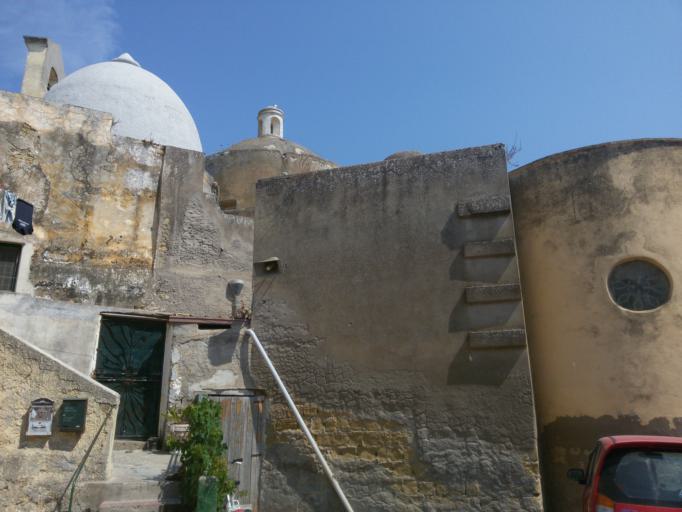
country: IT
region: Campania
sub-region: Provincia di Napoli
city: Procida
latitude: 40.7611
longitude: 14.0344
